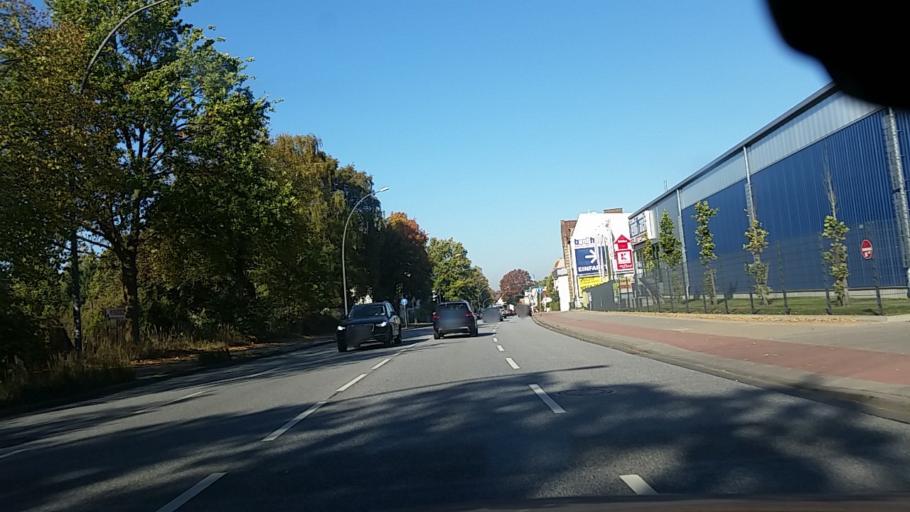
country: DE
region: Hamburg
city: Eidelstedt
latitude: 53.5824
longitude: 9.8822
